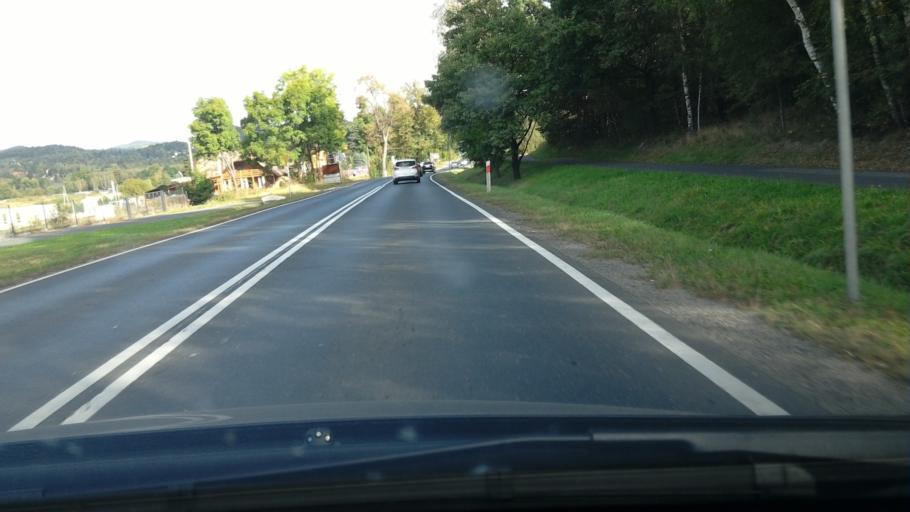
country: PL
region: Lower Silesian Voivodeship
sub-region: Jelenia Gora
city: Jelenia Gora
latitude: 50.8763
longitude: 15.7590
